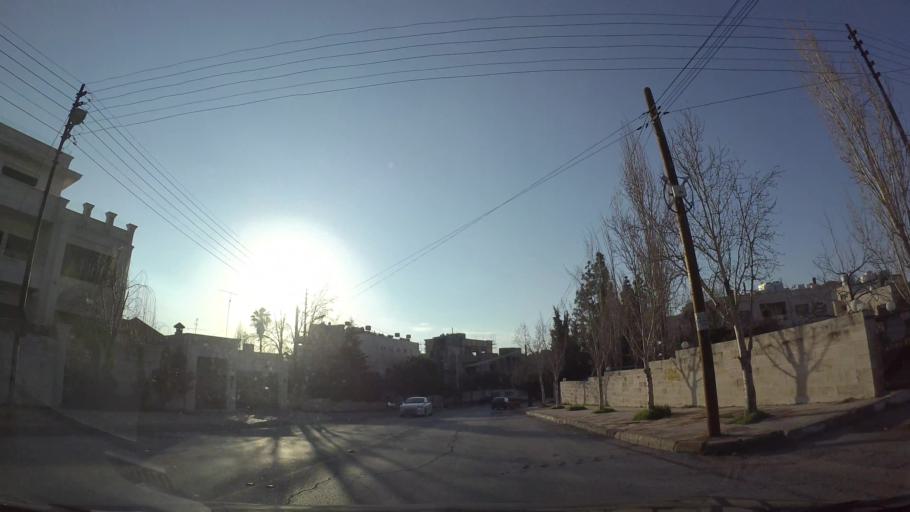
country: JO
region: Amman
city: Al Jubayhah
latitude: 31.9743
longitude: 35.8745
